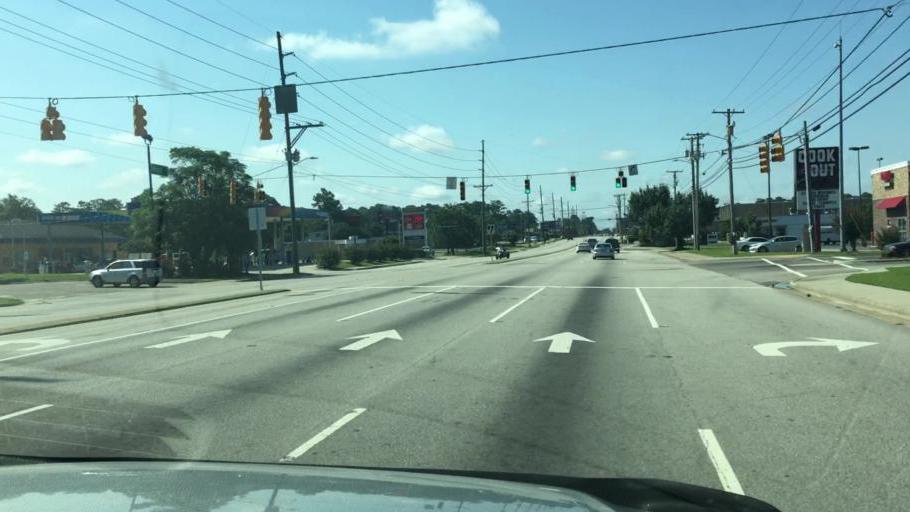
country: US
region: North Carolina
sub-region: Cumberland County
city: Fayetteville
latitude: 35.1128
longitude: -78.8797
